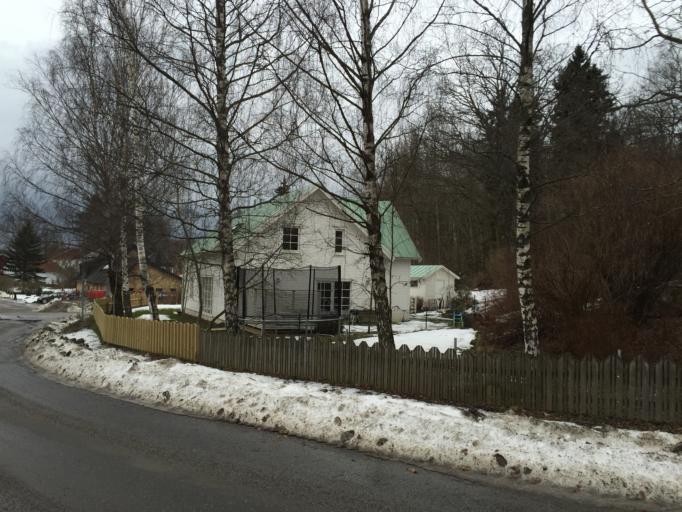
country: SE
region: Stockholm
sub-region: Salems Kommun
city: Ronninge
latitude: 59.2000
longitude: 17.7295
